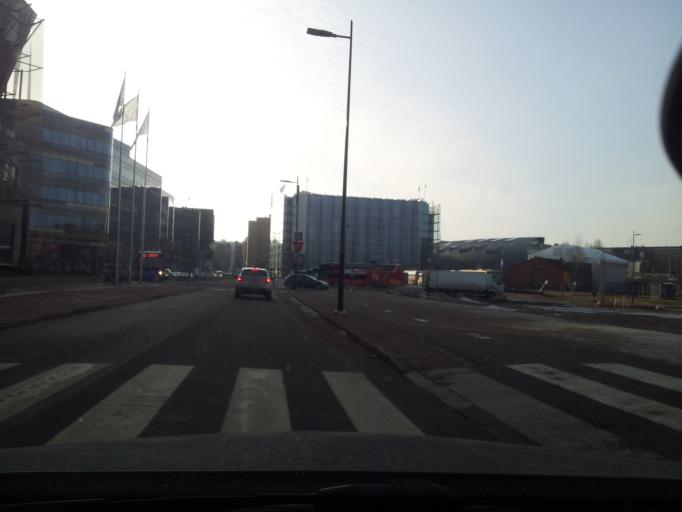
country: FI
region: Uusimaa
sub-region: Helsinki
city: Helsinki
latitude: 60.1751
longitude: 24.9383
